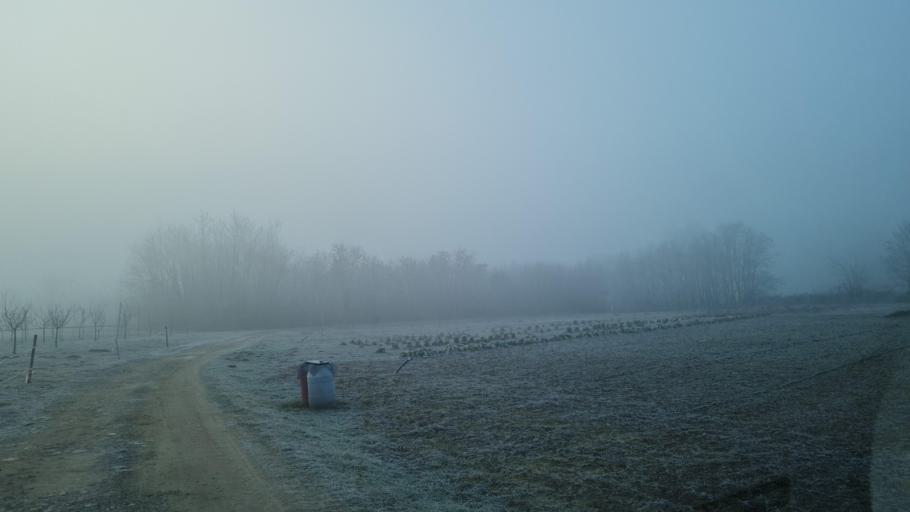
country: IT
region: Piedmont
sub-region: Provincia di Biella
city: Vergnasco
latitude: 45.4683
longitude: 8.0895
